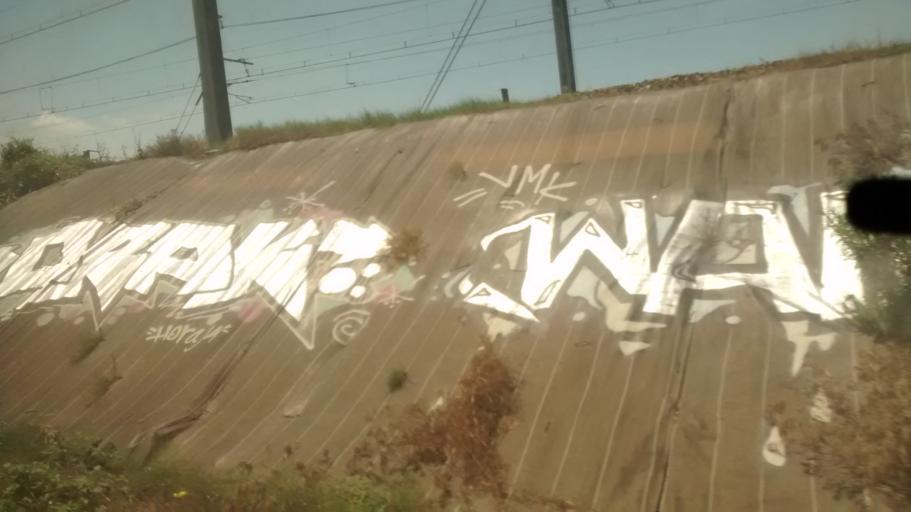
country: FR
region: Rhone-Alpes
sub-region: Departement du Rhone
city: Lyon
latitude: 45.7319
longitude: 4.8497
